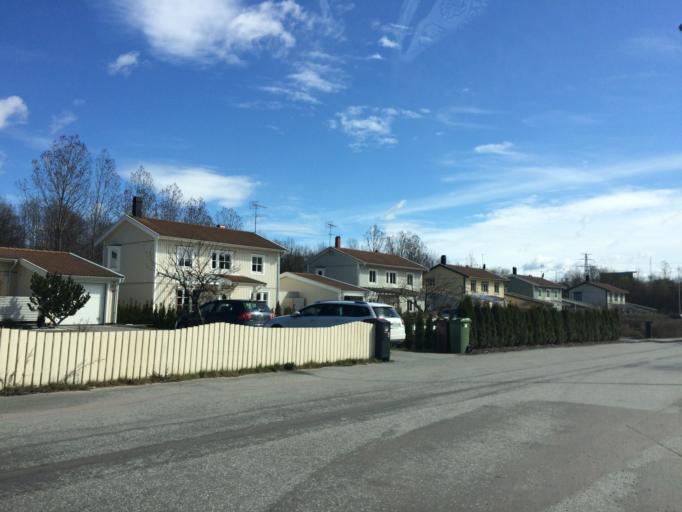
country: SE
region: Stockholm
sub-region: Sollentuna Kommun
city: Sollentuna
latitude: 59.4509
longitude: 17.9163
